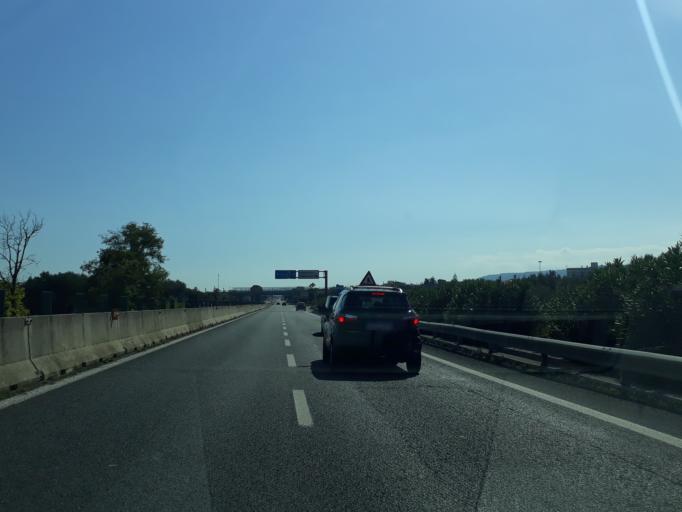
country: IT
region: Apulia
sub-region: Provincia di Bari
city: Monopoli
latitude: 40.8975
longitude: 17.3292
